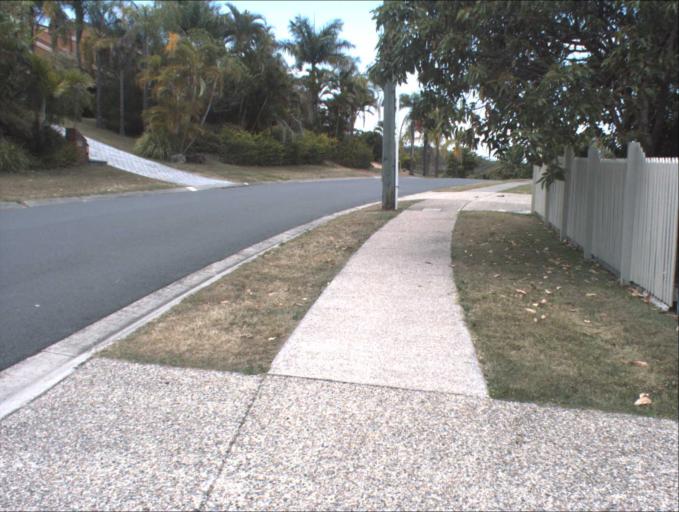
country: AU
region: Queensland
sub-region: Logan
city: Slacks Creek
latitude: -27.6538
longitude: 153.1828
